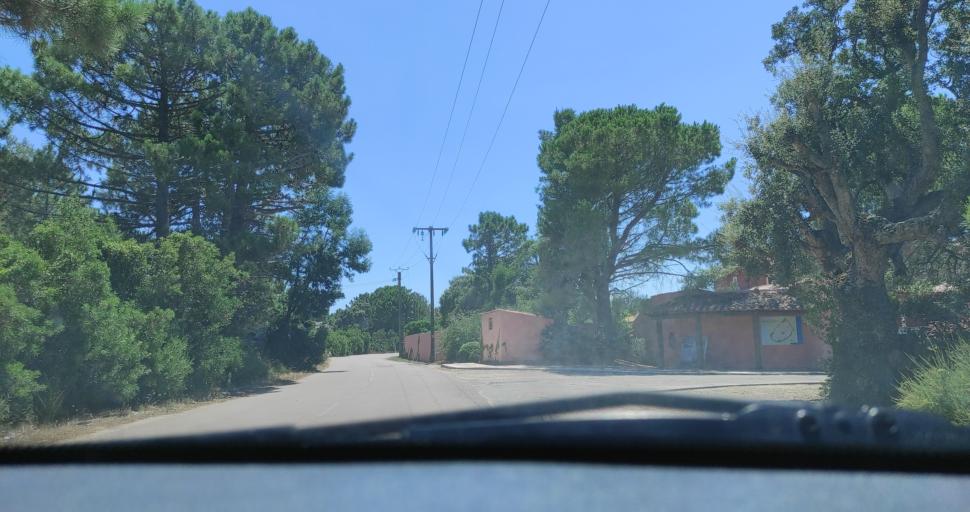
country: FR
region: Corsica
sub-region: Departement de la Corse-du-Sud
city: Porto-Vecchio
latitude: 41.6269
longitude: 9.3359
